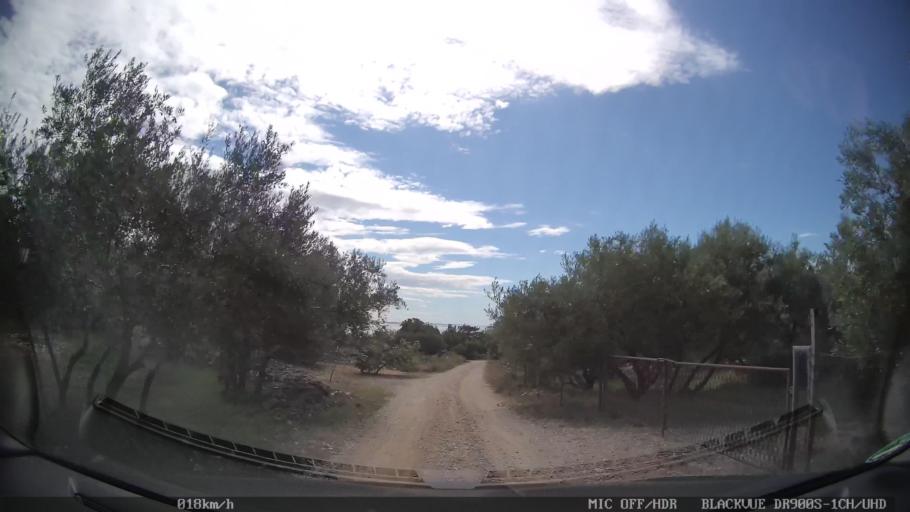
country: HR
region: Primorsko-Goranska
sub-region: Grad Krk
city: Krk
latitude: 45.0216
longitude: 14.5239
